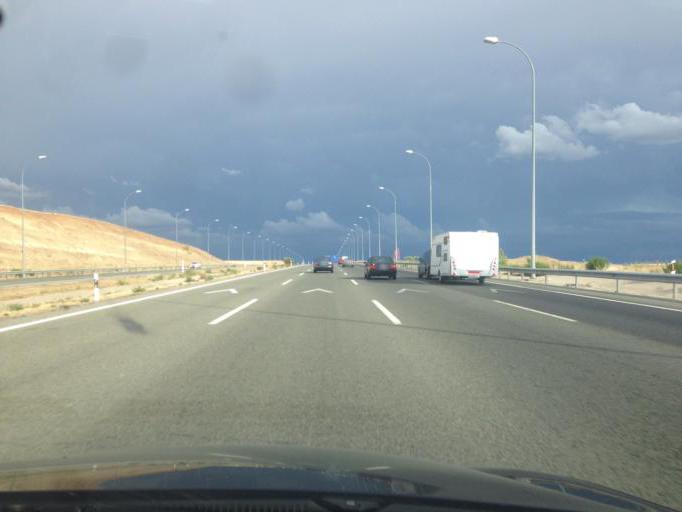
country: ES
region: Madrid
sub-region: Provincia de Madrid
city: Paracuellos de Jarama
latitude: 40.5339
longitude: -3.5234
